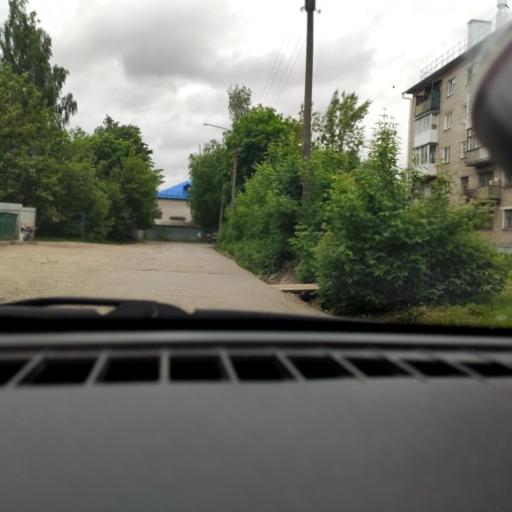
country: RU
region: Perm
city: Ust'-Kachka
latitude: 58.0049
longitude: 55.6701
